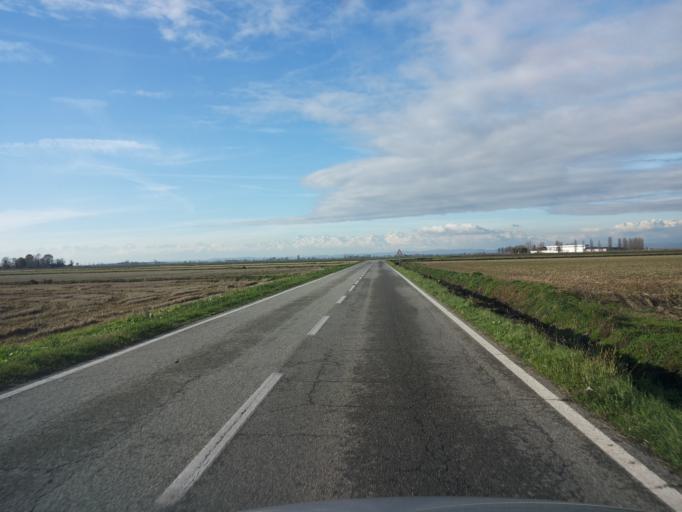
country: IT
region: Piedmont
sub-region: Provincia di Vercelli
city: Ronsecco
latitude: 45.2785
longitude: 8.2509
